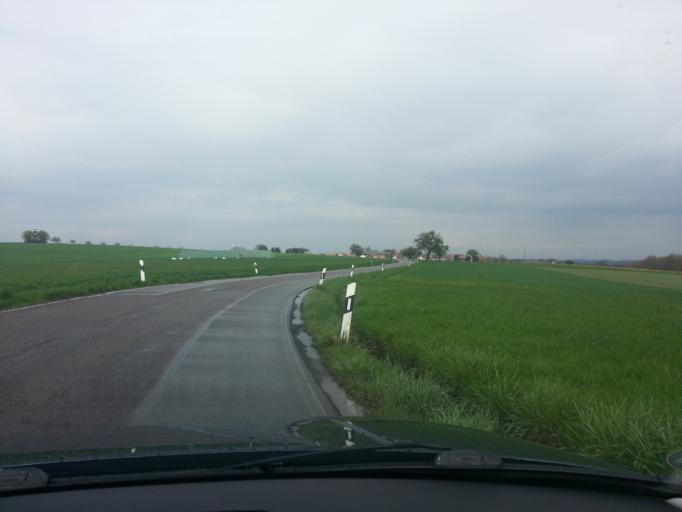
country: DE
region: Rheinland-Pfalz
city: Schmitshausen
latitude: 49.2984
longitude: 7.5121
